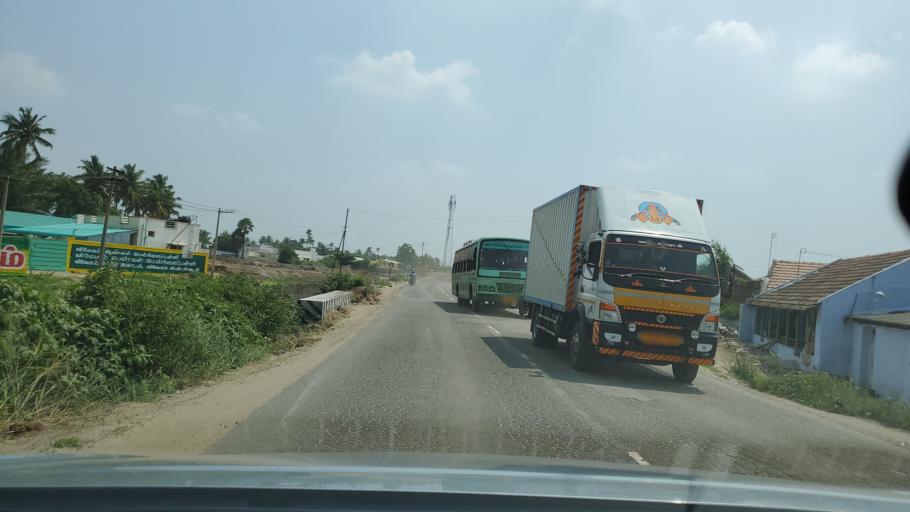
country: IN
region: Tamil Nadu
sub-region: Tiruppur
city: Dharapuram
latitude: 10.7706
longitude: 77.5117
